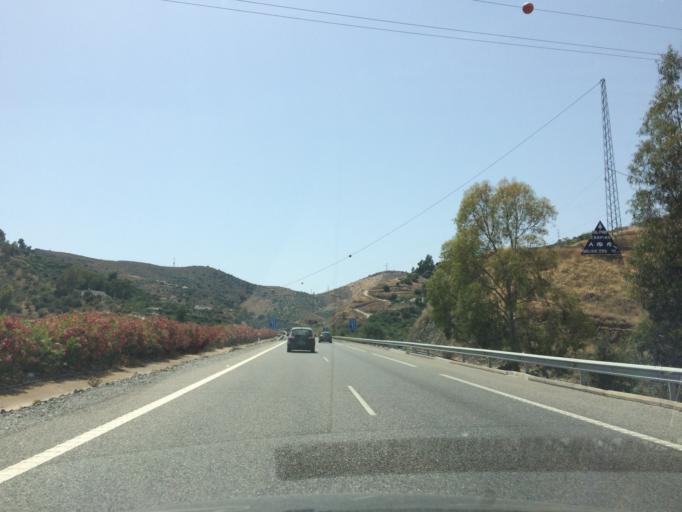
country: ES
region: Andalusia
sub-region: Provincia de Malaga
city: Frigiliana
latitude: 36.7572
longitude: -3.9102
